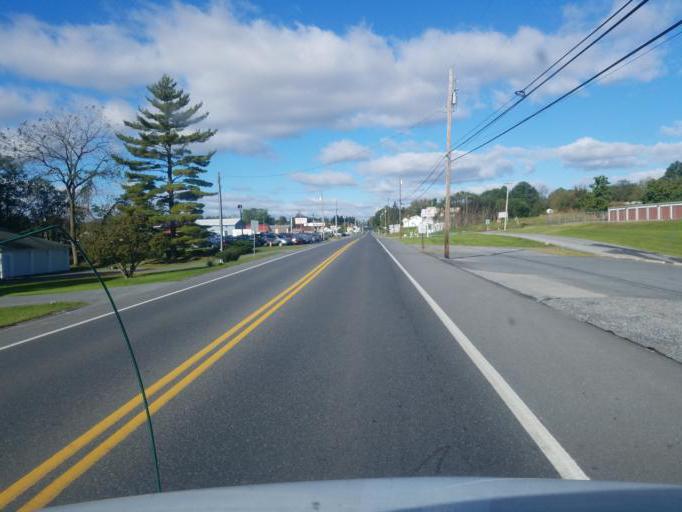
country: US
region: Pennsylvania
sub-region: Franklin County
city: Waynesboro
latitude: 39.7673
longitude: -77.6188
